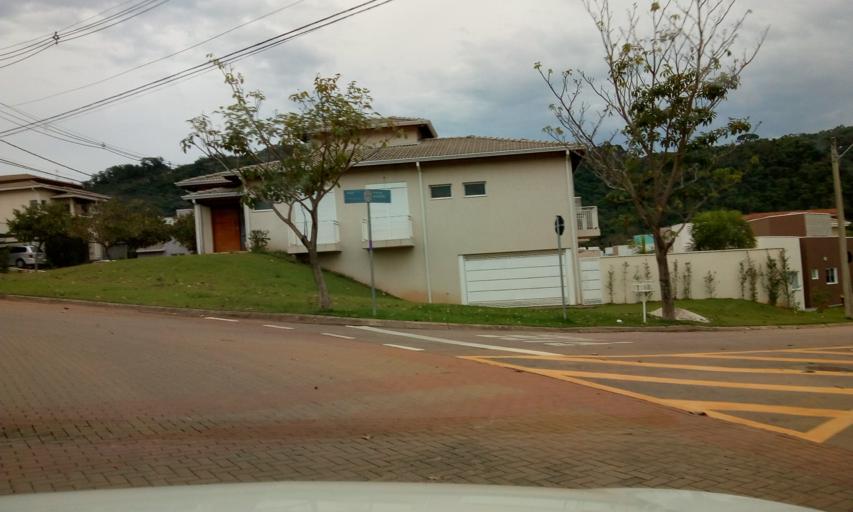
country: BR
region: Sao Paulo
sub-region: Itupeva
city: Itupeva
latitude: -23.1381
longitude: -47.0500
